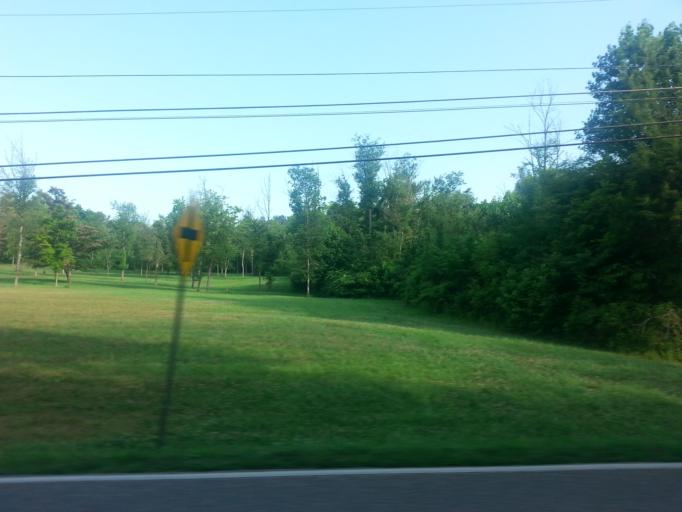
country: US
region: Tennessee
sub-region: Blount County
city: Louisville
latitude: 35.8213
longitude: -84.0515
